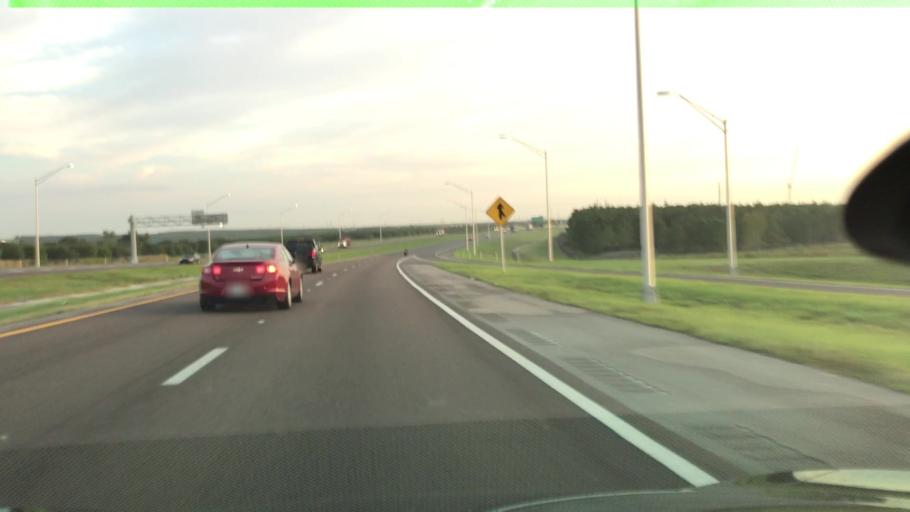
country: US
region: Florida
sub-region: Orange County
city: Oakland
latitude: 28.4529
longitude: -81.6412
